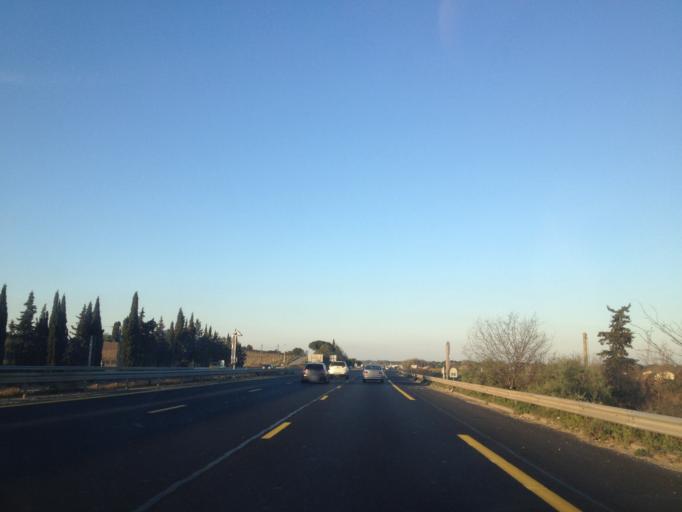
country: FR
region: Languedoc-Roussillon
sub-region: Departement de l'Herault
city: Saint-Aunes
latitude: 43.6169
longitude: 3.9480
